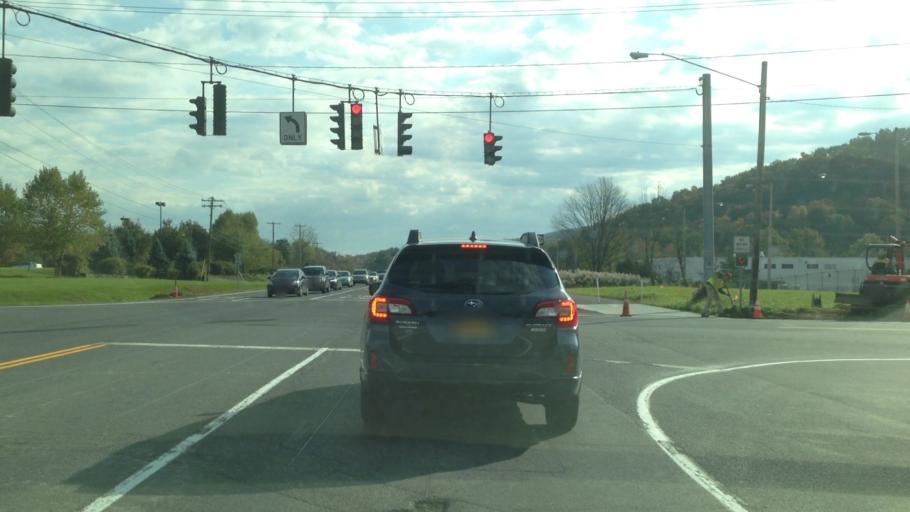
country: US
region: New York
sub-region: Ulster County
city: Clintondale
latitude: 41.7379
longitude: -74.0370
